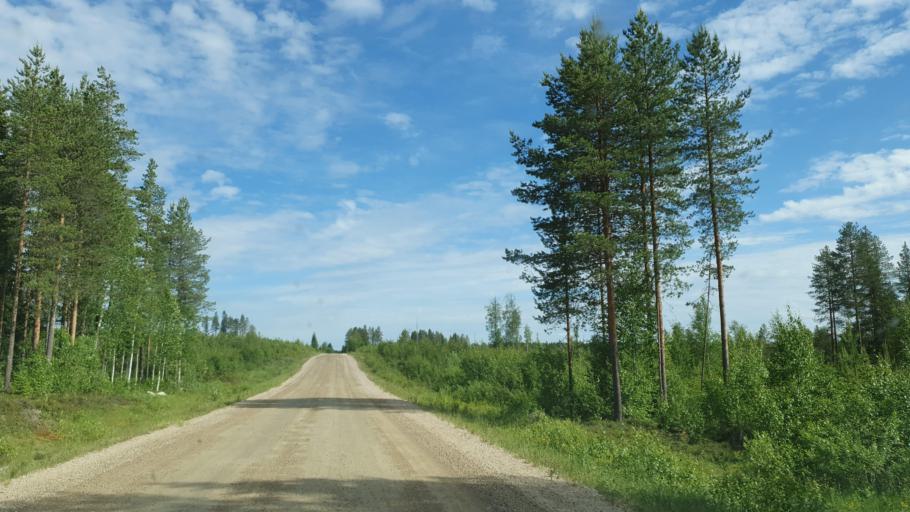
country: FI
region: Kainuu
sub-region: Kehys-Kainuu
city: Kuhmo
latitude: 64.5116
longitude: 29.4591
